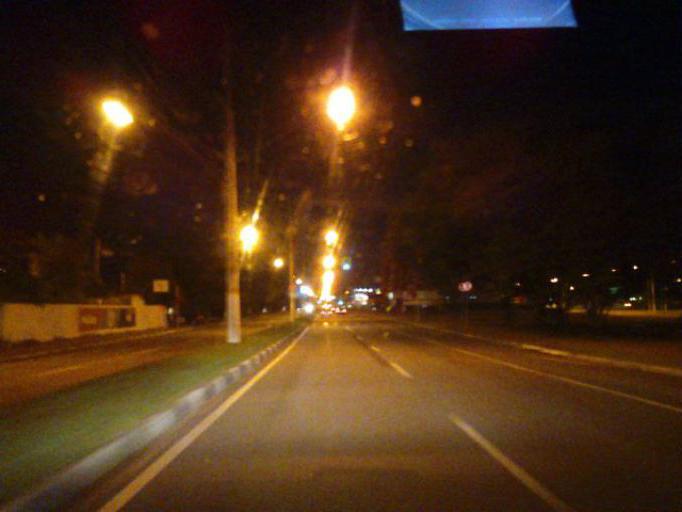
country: BR
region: Sao Paulo
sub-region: Jacarei
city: Jacarei
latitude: -23.2842
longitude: -45.9524
